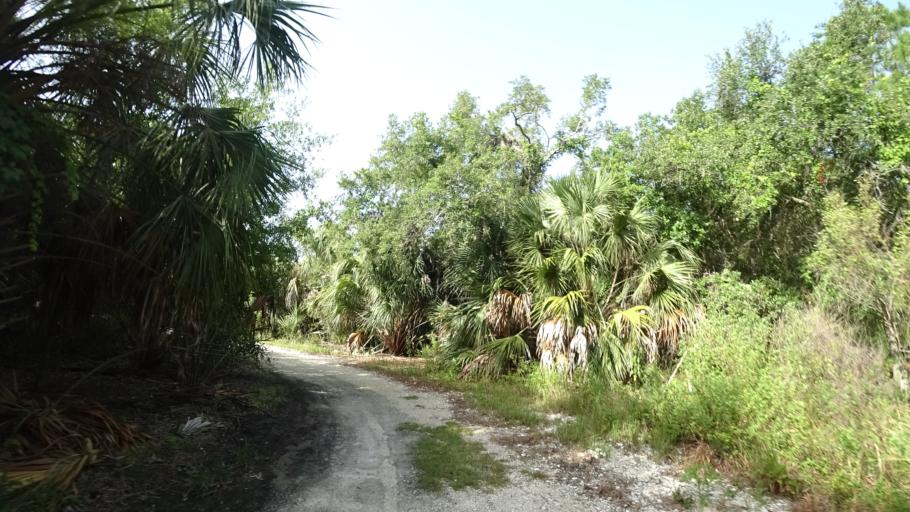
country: US
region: Florida
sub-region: Manatee County
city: West Bradenton
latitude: 27.5316
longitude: -82.6227
